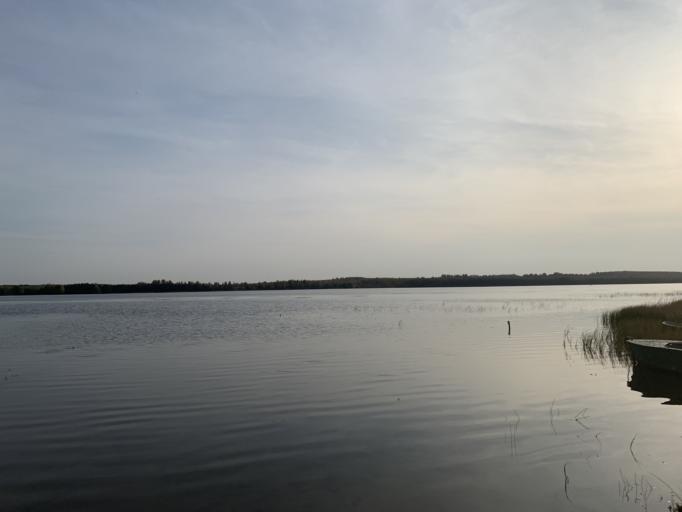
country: RU
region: Jaroslavl
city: Porech'ye-Rybnoye
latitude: 56.9783
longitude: 39.3863
